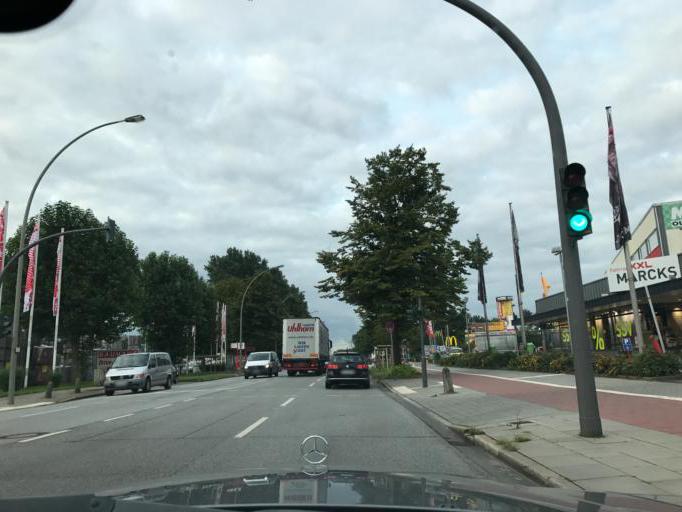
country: DE
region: Hamburg
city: Bergedorf
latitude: 53.4816
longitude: 10.2084
